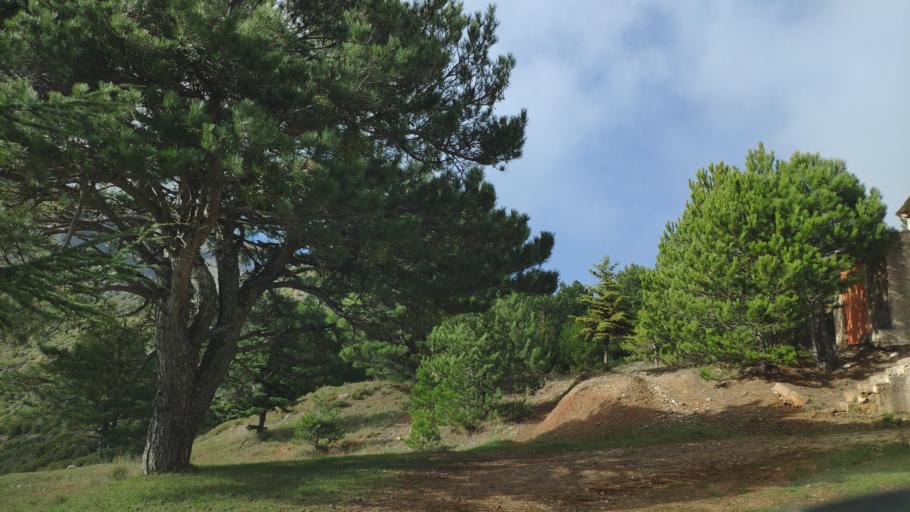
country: GR
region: West Greece
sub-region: Nomos Achaias
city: Aiyira
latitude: 38.0563
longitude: 22.4409
